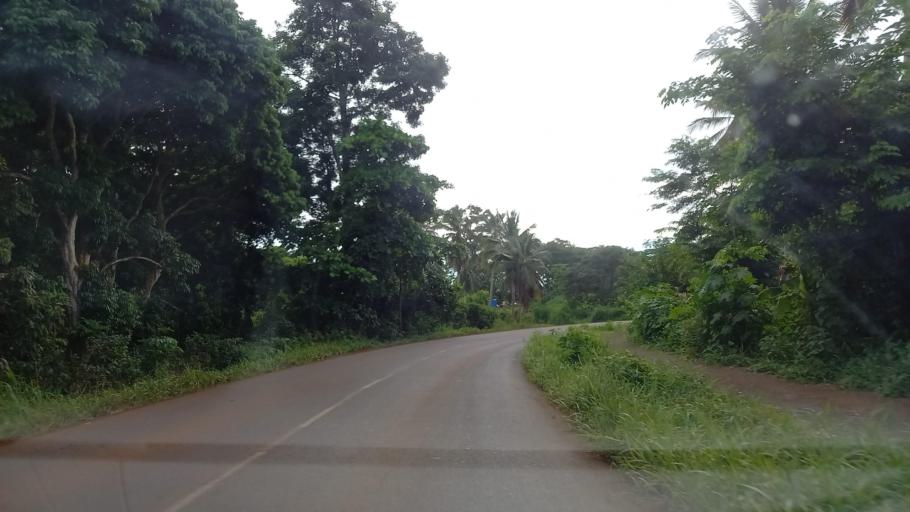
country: YT
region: Tsingoni
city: Tsingoni
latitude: -12.7935
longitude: 45.1226
